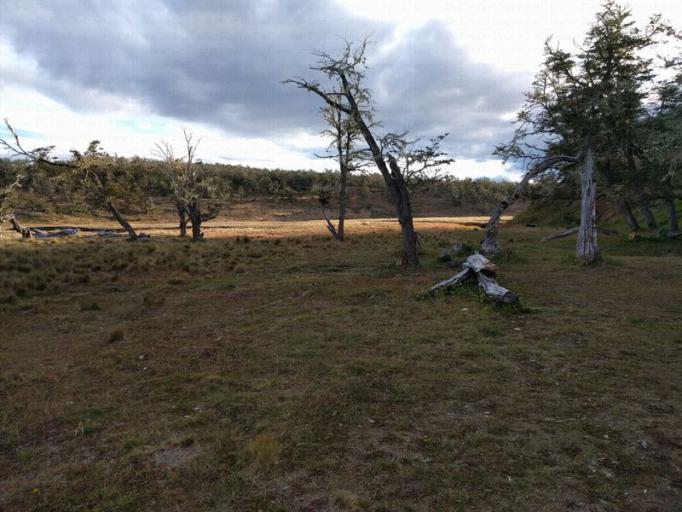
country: AR
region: Tierra del Fuego
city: Rio Grande
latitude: -54.2057
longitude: -67.2253
